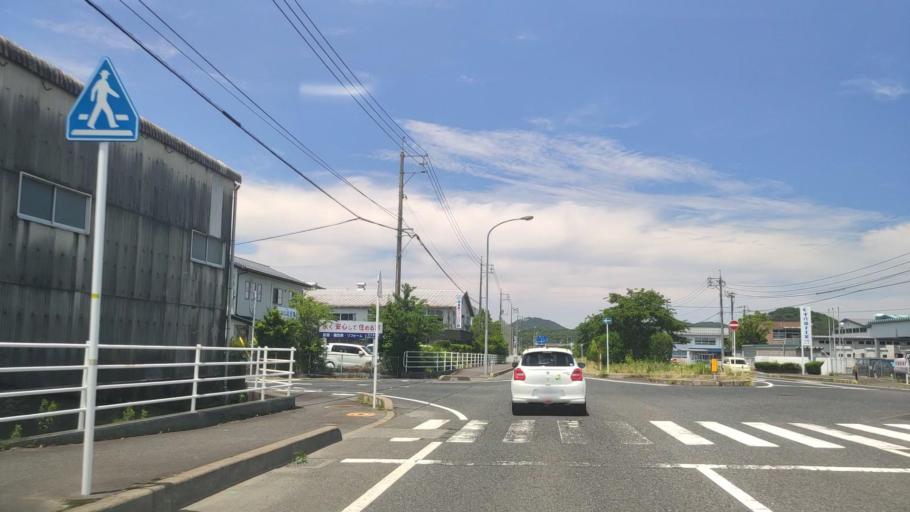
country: JP
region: Tottori
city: Tottori
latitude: 35.4596
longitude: 134.2430
